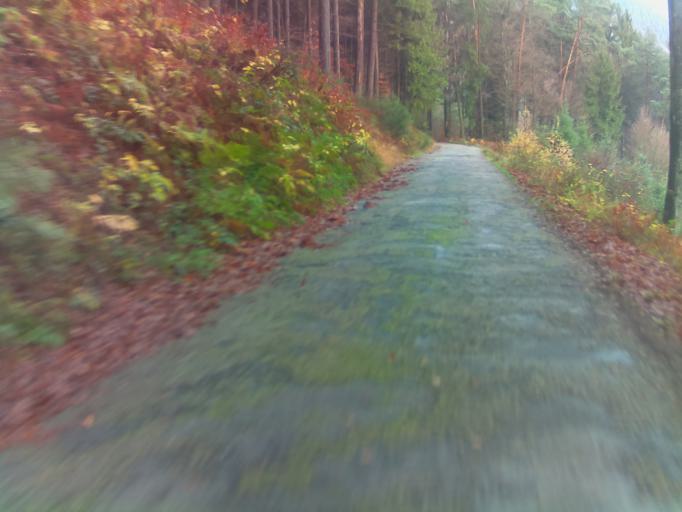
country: DE
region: Baden-Wuerttemberg
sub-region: Karlsruhe Region
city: Heddesbach
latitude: 49.4896
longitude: 8.8477
